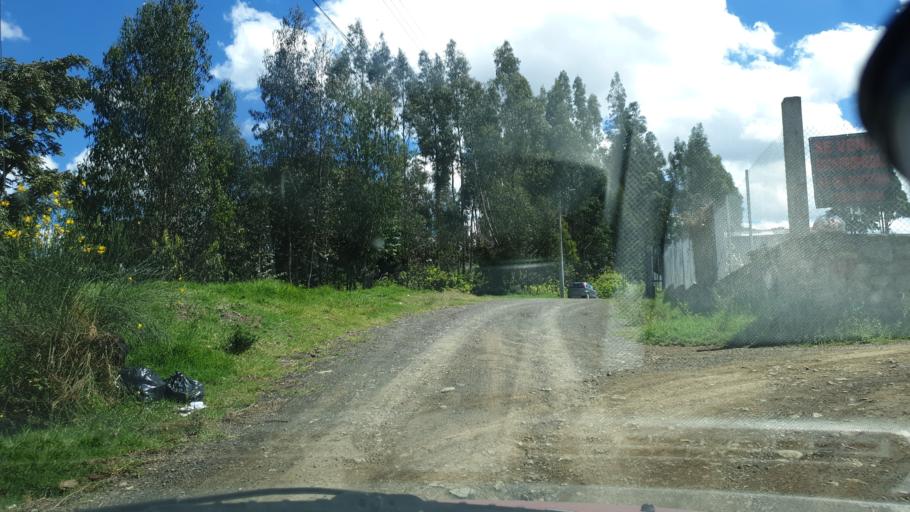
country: EC
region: Azuay
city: Cuenca
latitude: -2.8747
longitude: -78.9515
